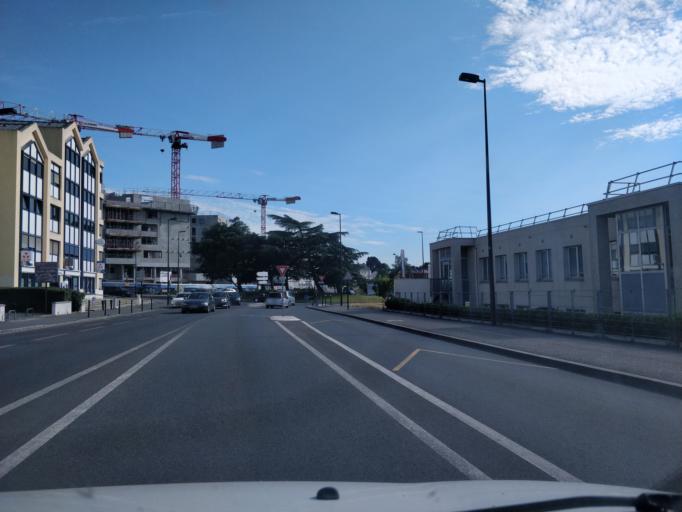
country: FR
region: Pays de la Loire
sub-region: Departement de la Loire-Atlantique
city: Nantes
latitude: 47.2435
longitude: -1.5339
